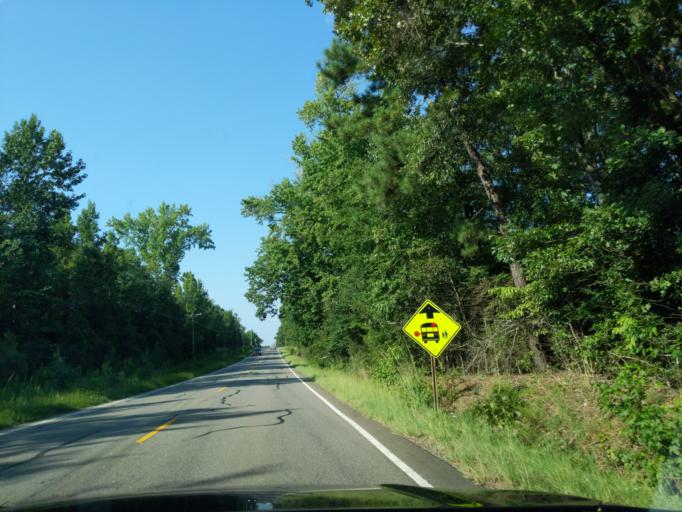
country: US
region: South Carolina
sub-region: Newberry County
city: Prosperity
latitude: 34.1091
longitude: -81.5635
